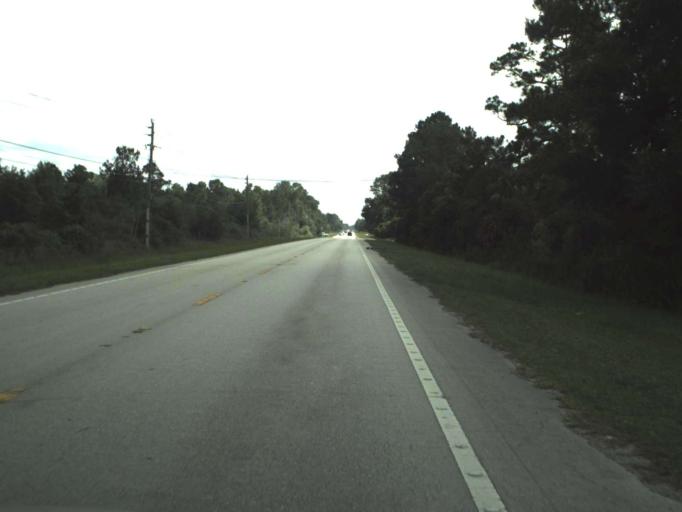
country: US
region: Florida
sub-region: Volusia County
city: Samsula-Spruce Creek
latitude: 28.9890
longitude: -81.0723
